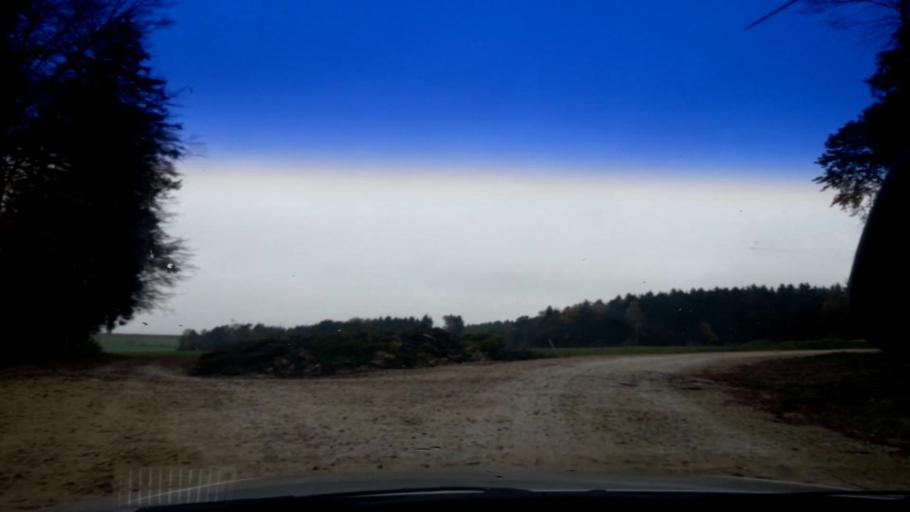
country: DE
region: Bavaria
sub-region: Upper Franconia
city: Wattendorf
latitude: 50.0255
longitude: 11.1473
